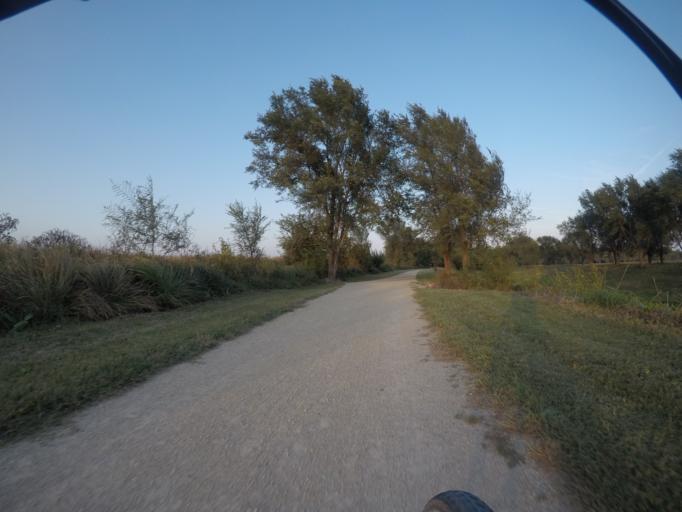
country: US
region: Kansas
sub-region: Riley County
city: Manhattan
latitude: 39.1984
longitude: -96.5467
